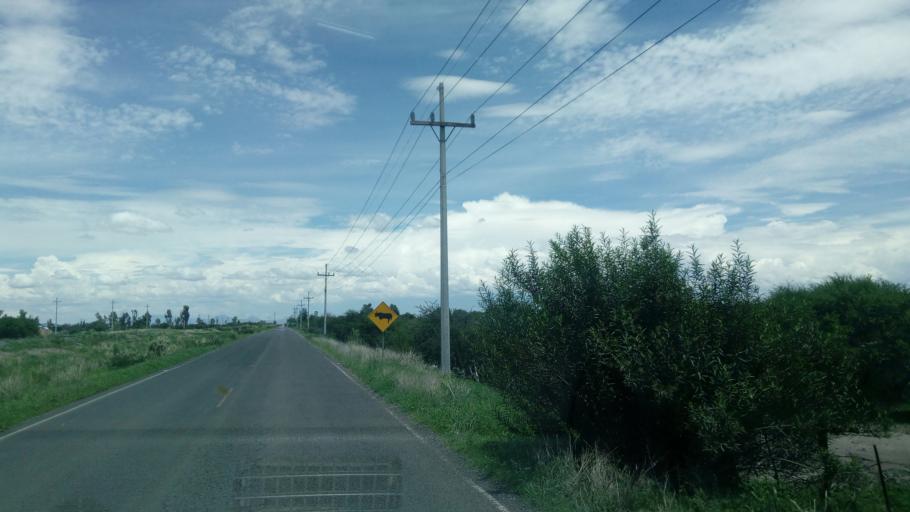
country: MX
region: Durango
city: Victoria de Durango
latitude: 24.1345
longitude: -104.5425
